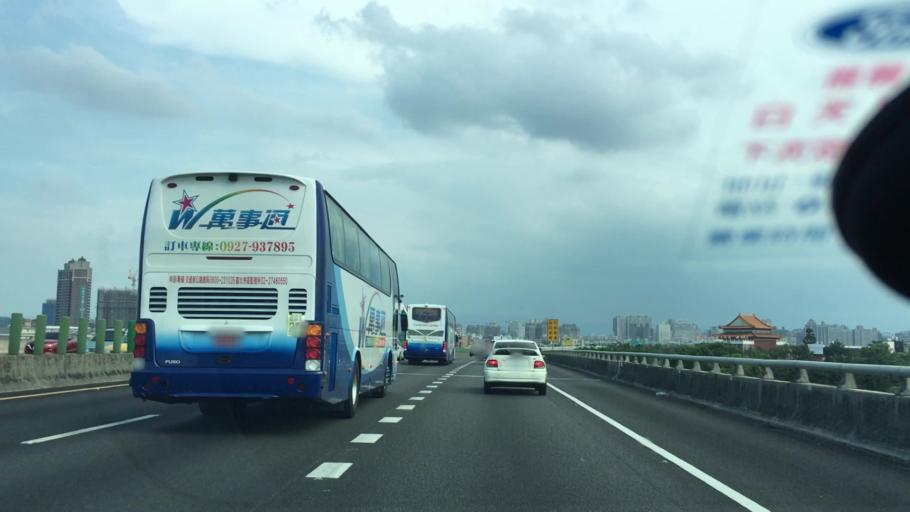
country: TW
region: Taiwan
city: Taoyuan City
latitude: 25.0091
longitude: 121.2808
